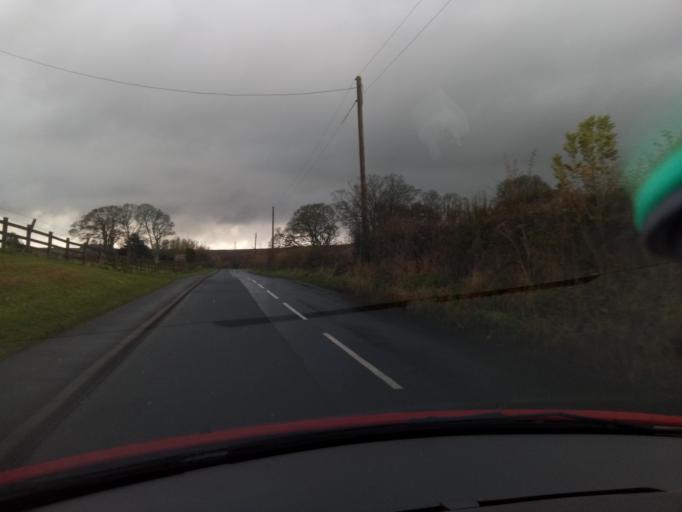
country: GB
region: England
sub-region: Northumberland
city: Birtley
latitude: 55.1422
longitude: -2.2619
